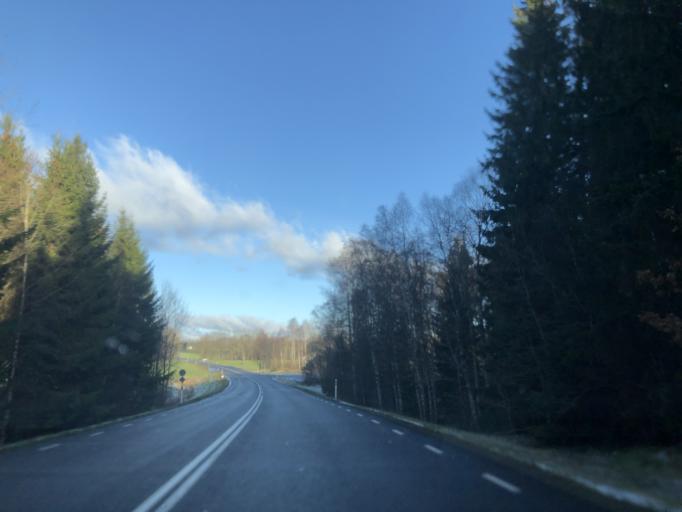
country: SE
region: Vaestra Goetaland
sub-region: Tranemo Kommun
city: Limmared
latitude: 57.6303
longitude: 13.4471
